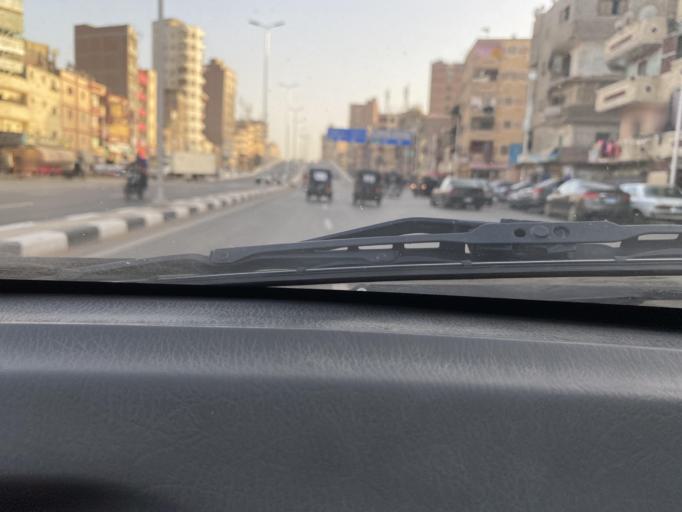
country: EG
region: Muhafazat al Qahirah
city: Cairo
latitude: 30.1239
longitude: 31.2972
